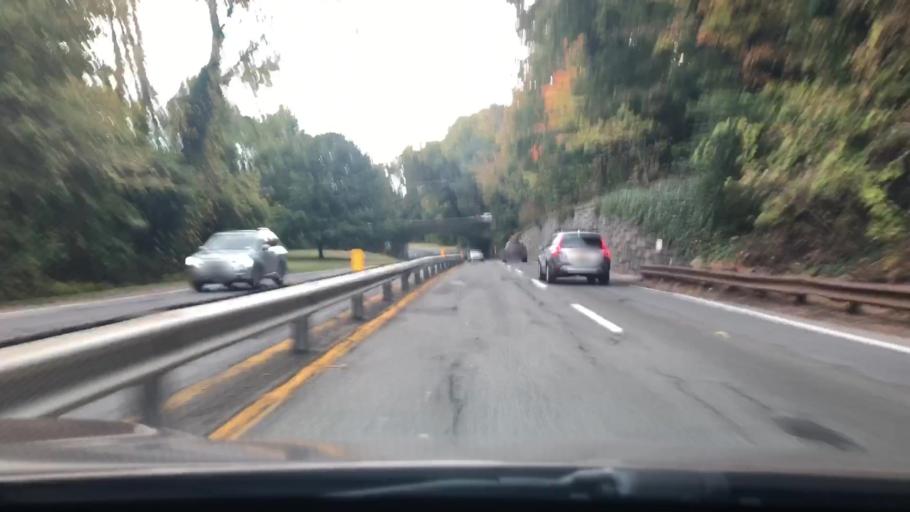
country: US
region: New York
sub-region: Westchester County
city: Tuckahoe
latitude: 40.9506
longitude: -73.8335
